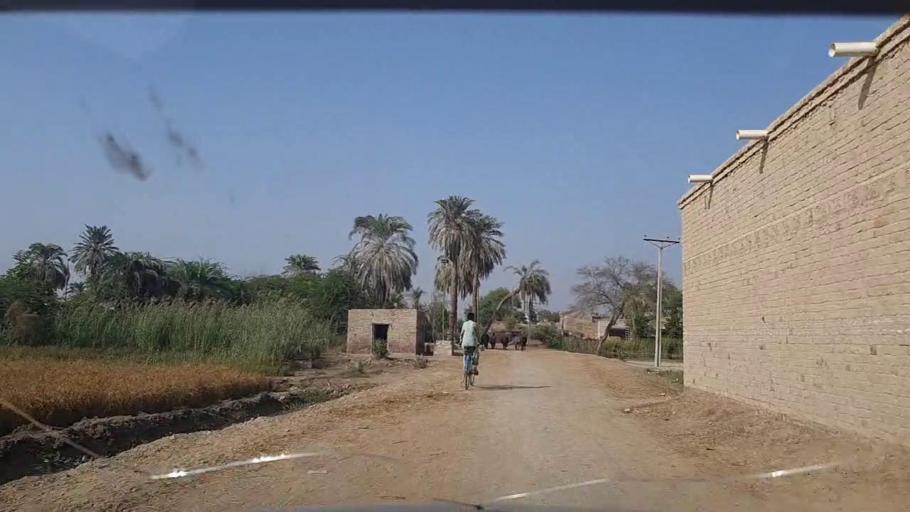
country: PK
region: Sindh
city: Shikarpur
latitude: 28.1199
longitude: 68.5786
